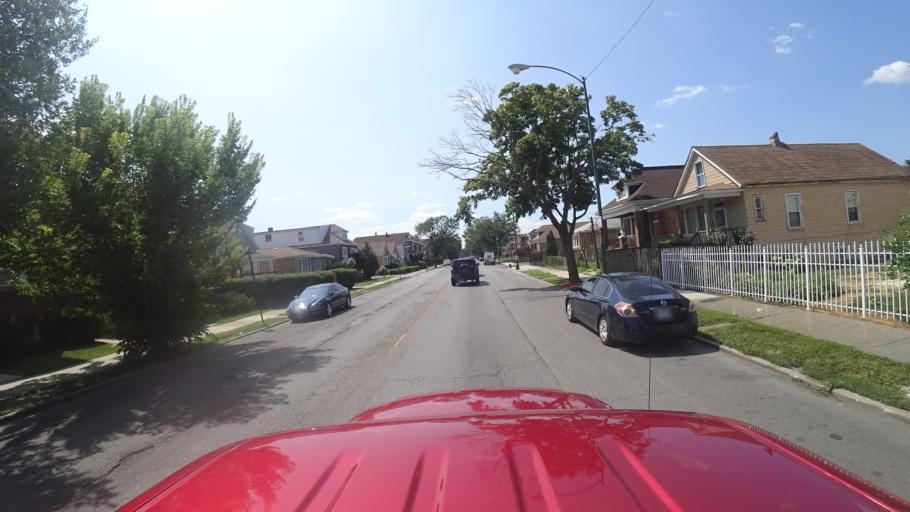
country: US
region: Illinois
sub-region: Cook County
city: Chicago
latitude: 41.7980
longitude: -87.6940
